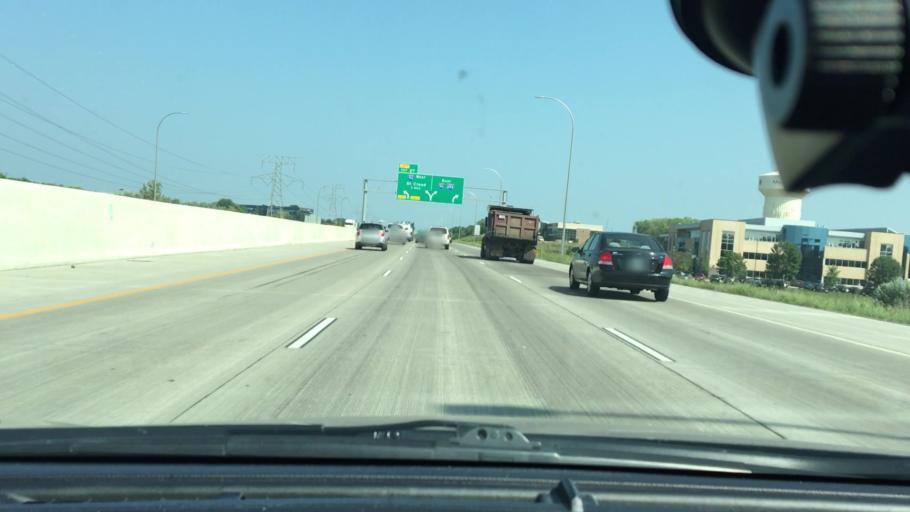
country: US
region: Minnesota
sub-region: Hennepin County
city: Maple Grove
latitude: 45.0736
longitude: -93.4459
